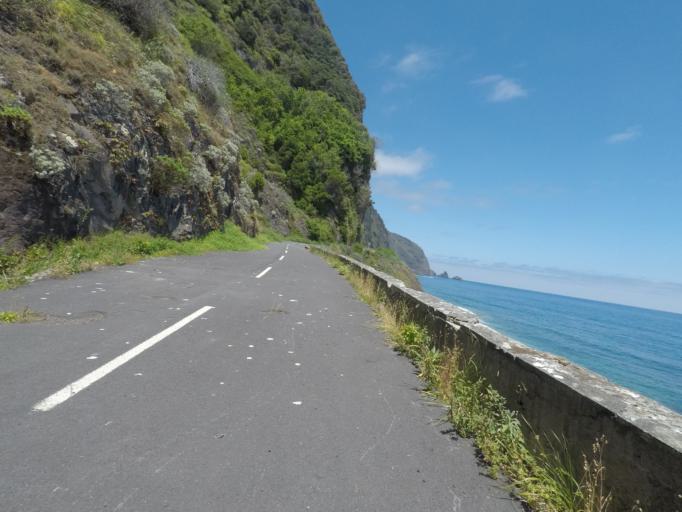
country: PT
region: Madeira
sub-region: Porto Moniz
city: Porto Moniz
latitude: 32.8289
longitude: -17.1275
